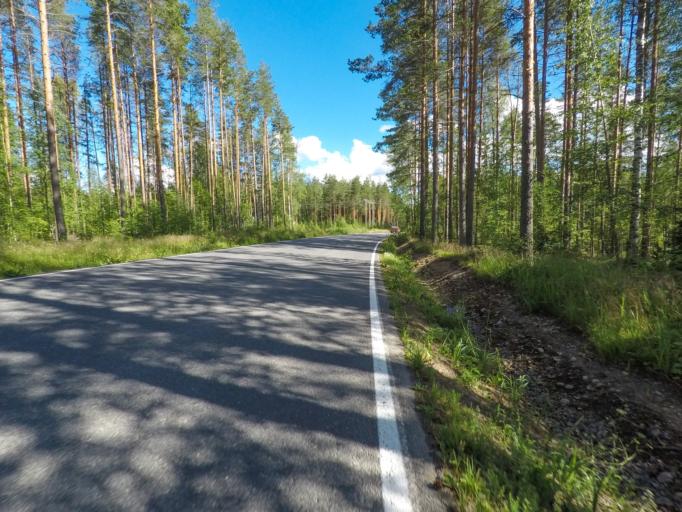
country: FI
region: South Karelia
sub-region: Lappeenranta
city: Taipalsaari
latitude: 61.1764
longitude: 28.0128
